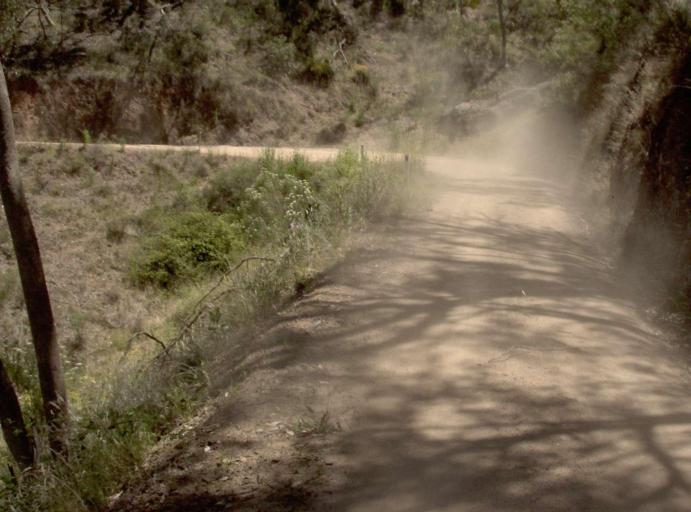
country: AU
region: New South Wales
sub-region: Snowy River
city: Jindabyne
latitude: -37.0840
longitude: 148.3936
